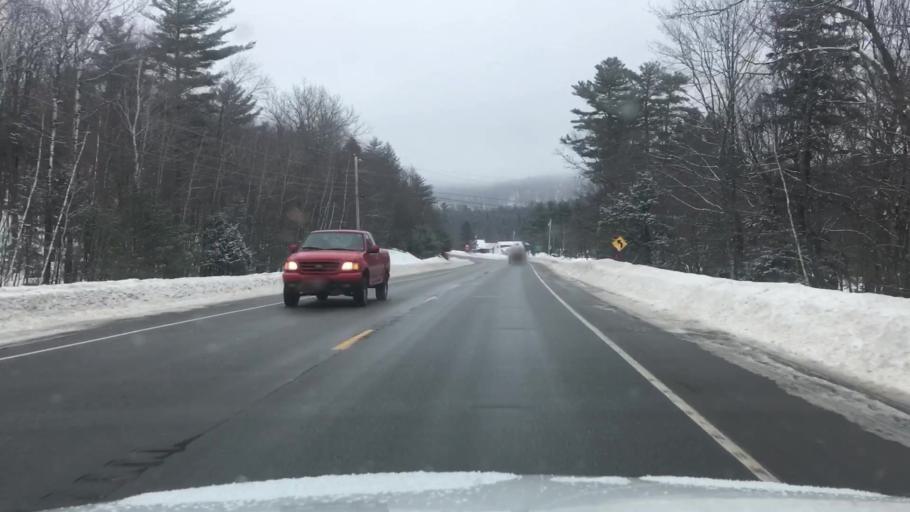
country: US
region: Maine
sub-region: Franklin County
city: Wilton
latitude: 44.5784
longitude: -70.3303
